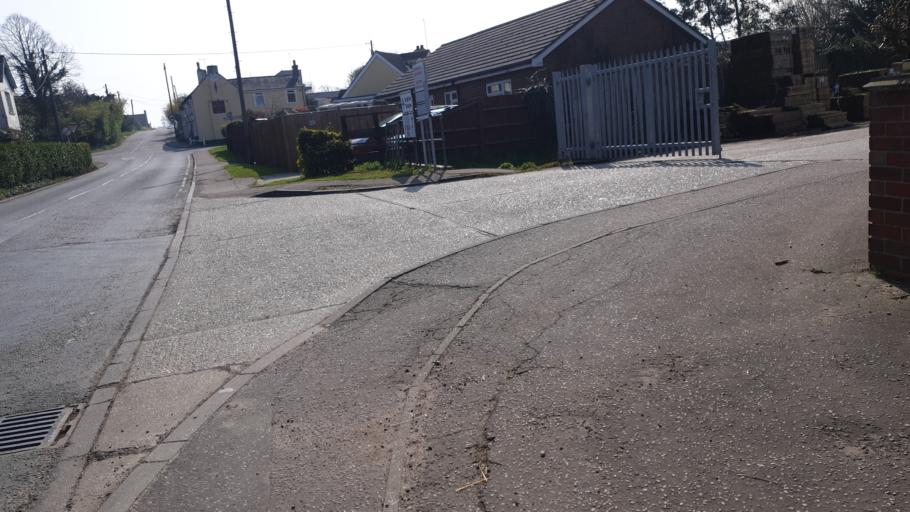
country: GB
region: England
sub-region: Essex
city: Mistley
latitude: 51.9130
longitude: 1.1430
